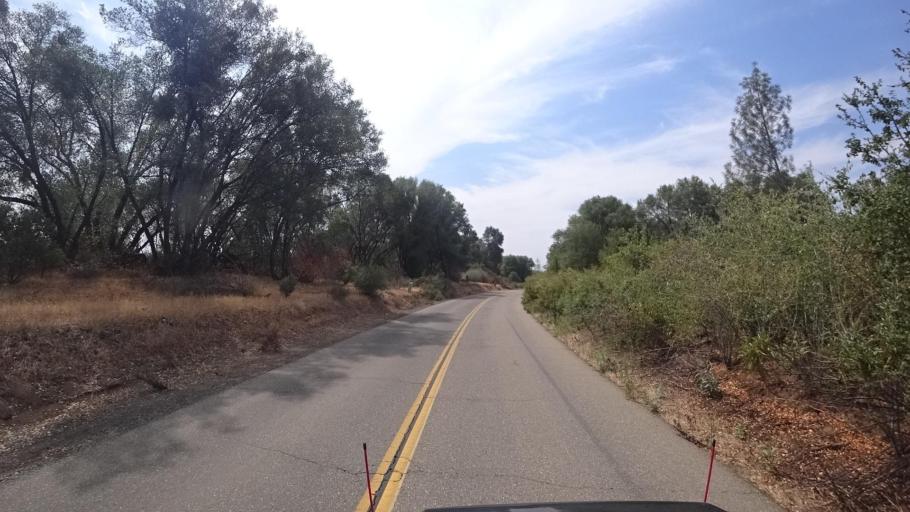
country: US
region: California
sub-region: Mariposa County
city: Midpines
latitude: 37.5003
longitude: -119.8899
